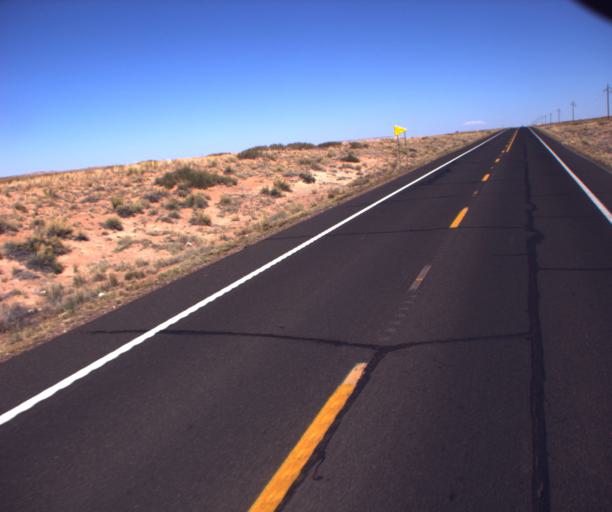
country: US
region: Arizona
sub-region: Coconino County
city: Tuba City
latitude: 36.1393
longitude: -111.1650
